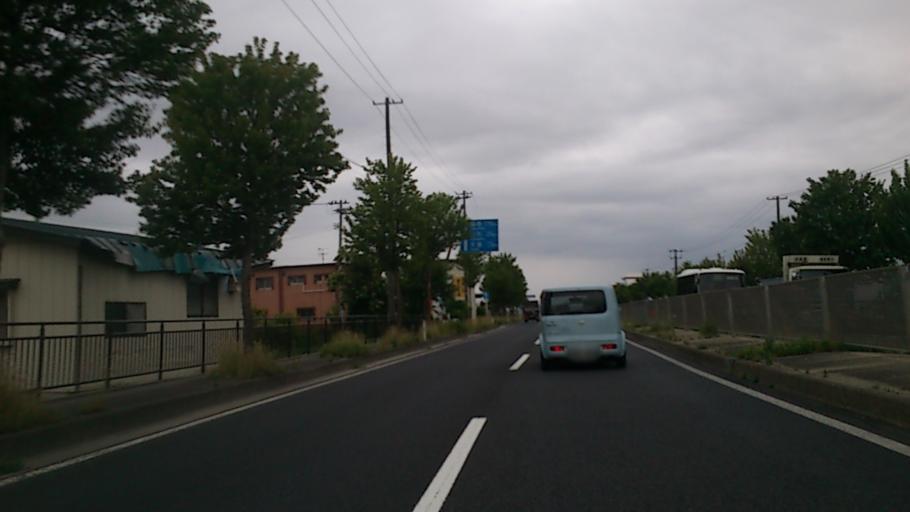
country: JP
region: Yamagata
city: Higashine
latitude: 38.4736
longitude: 140.3829
